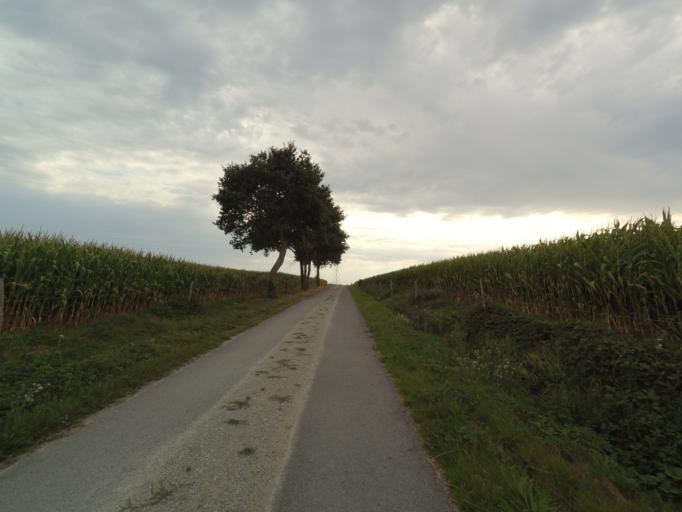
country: FR
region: Pays de la Loire
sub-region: Departement de la Vendee
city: Bouffere
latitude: 46.9808
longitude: -1.3611
